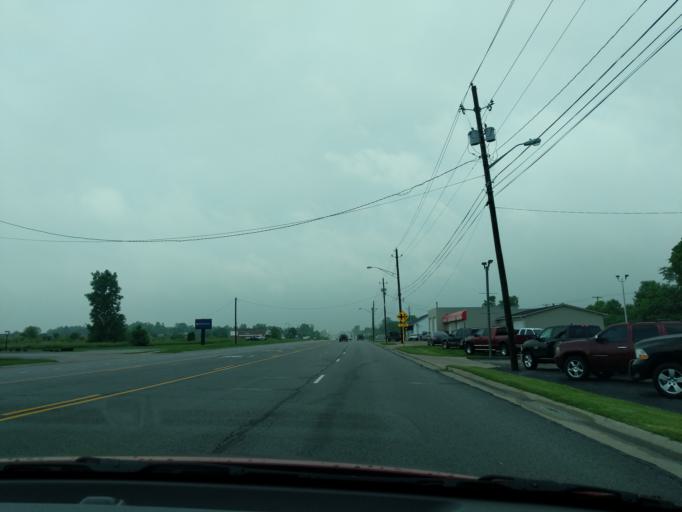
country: US
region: Indiana
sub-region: Hancock County
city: McCordsville
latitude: 39.8924
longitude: -85.9271
